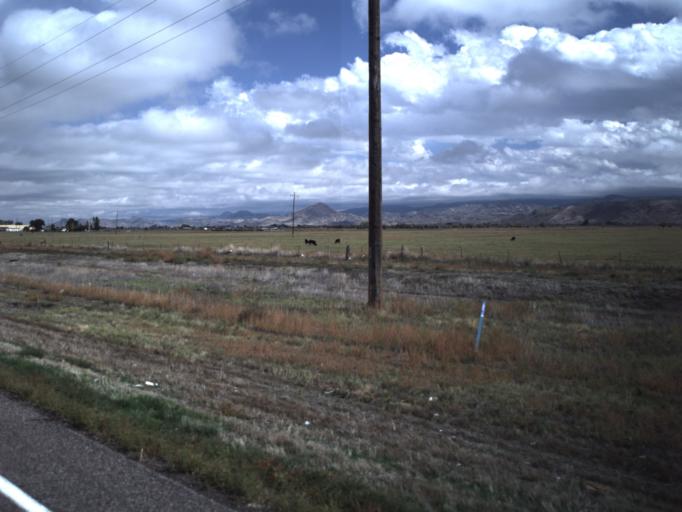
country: US
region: Utah
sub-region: Sevier County
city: Richfield
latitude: 38.7390
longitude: -112.0930
